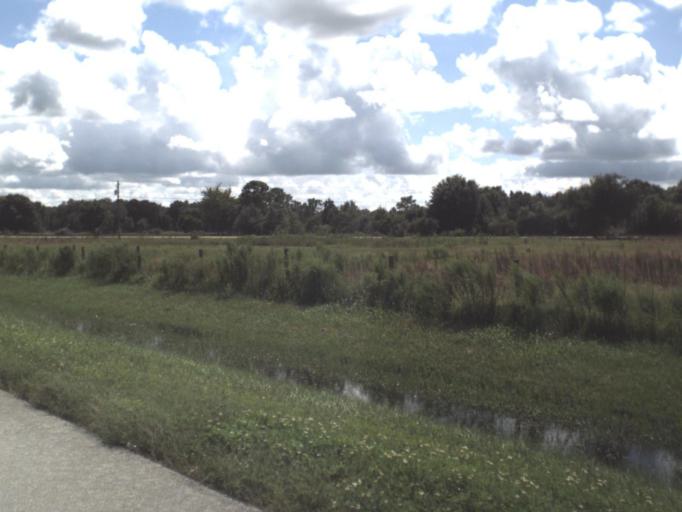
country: US
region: Florida
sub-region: DeSoto County
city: Arcadia
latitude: 27.2365
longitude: -81.9373
